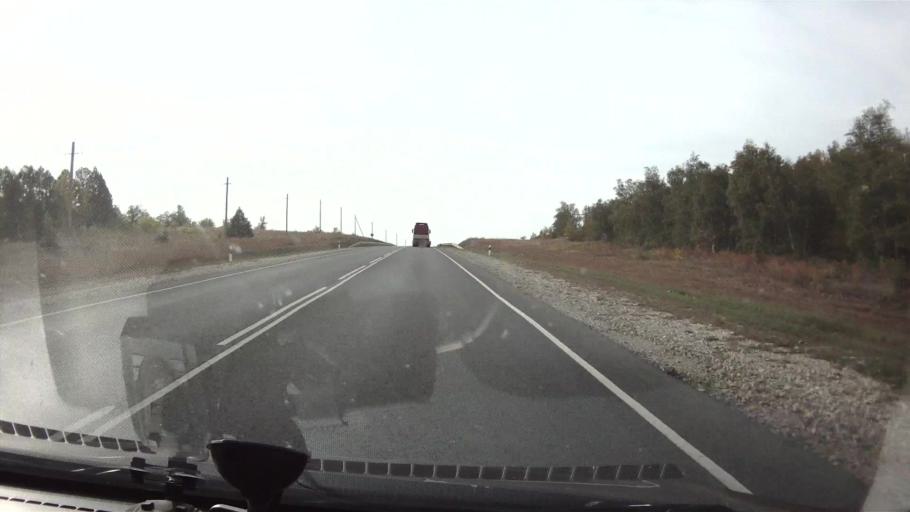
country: RU
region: Saratov
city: Shikhany
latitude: 52.1603
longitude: 47.1194
